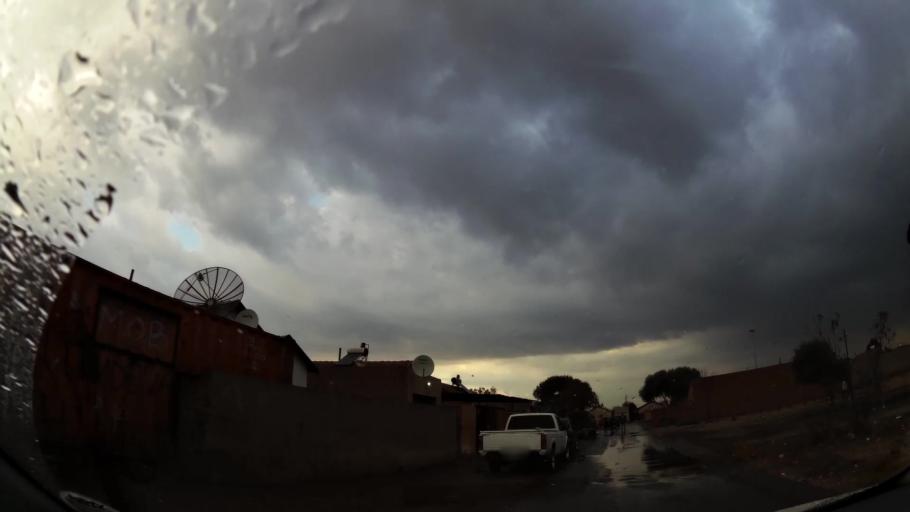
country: ZA
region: Gauteng
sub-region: Ekurhuleni Metropolitan Municipality
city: Germiston
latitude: -26.3623
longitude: 28.1305
